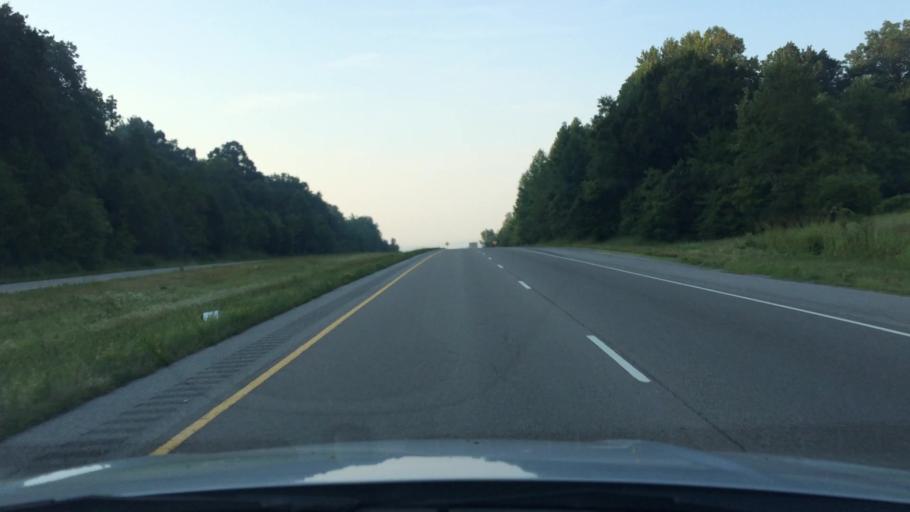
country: US
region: Tennessee
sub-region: Giles County
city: Pulaski
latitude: 35.1803
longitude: -87.0613
